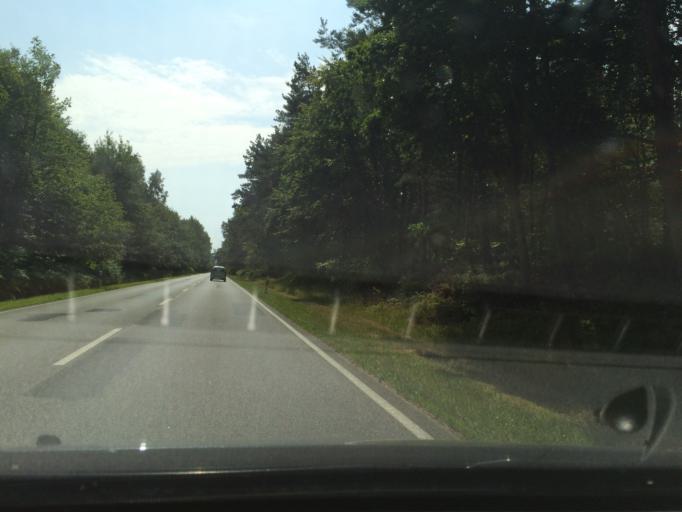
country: DE
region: Mecklenburg-Vorpommern
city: Ostseebad Binz
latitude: 54.4221
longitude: 13.5820
